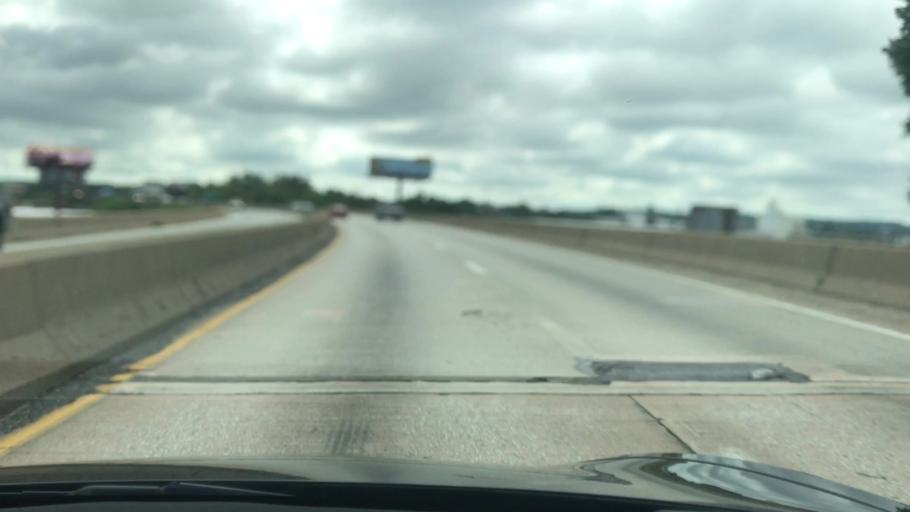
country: US
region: Pennsylvania
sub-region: York County
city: North York
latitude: 39.9798
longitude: -76.7260
